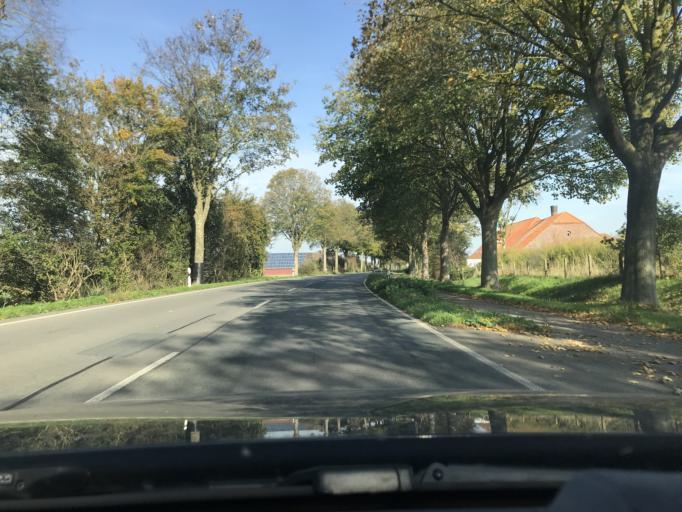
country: DE
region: North Rhine-Westphalia
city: Kalkar
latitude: 51.7250
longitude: 6.2665
